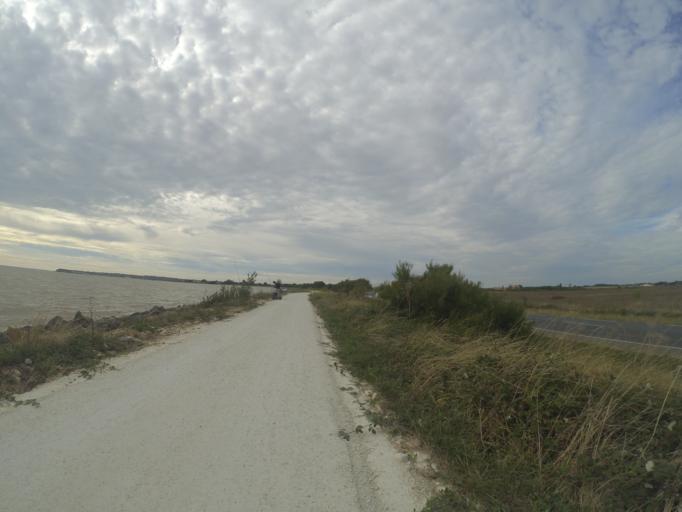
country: FR
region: Poitou-Charentes
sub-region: Departement de la Charente-Maritime
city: Meschers-sur-Gironde
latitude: 45.5470
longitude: -0.9126
